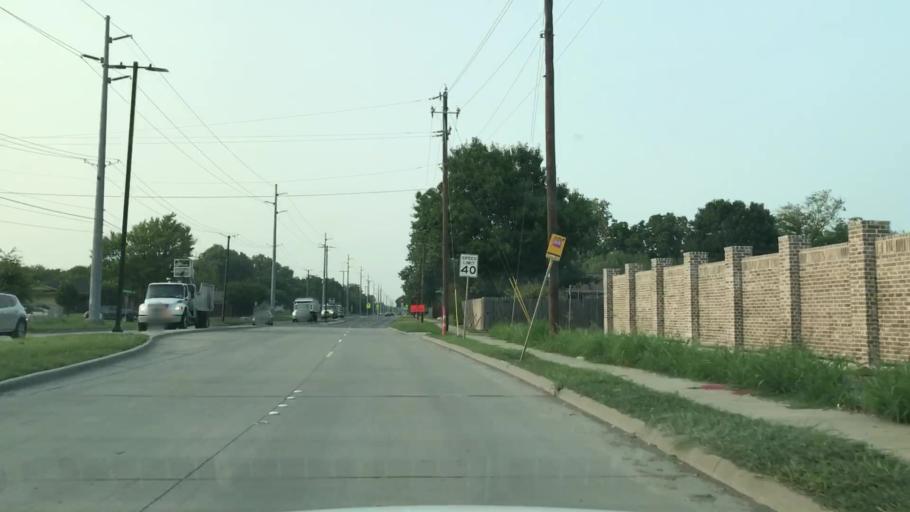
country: US
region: Texas
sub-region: Dallas County
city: Garland
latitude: 32.9150
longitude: -96.6136
